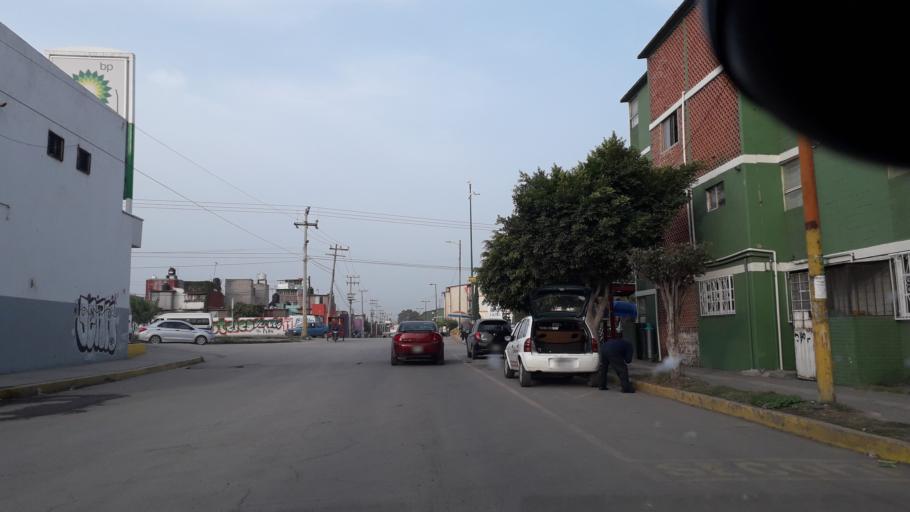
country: MX
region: Mexico
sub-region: Jaltenco
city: Alborada Jaltenco
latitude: 19.6590
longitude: -99.0690
